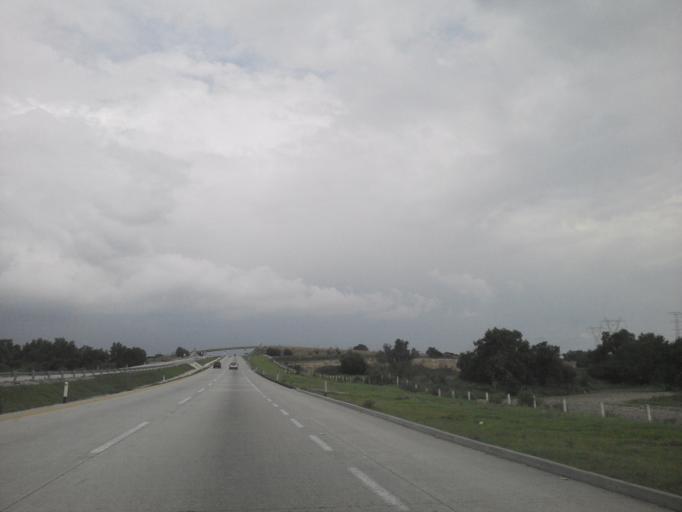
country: MX
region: Mexico
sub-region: Apaxco
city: Colonia Juarez
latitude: 19.9827
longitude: -99.1202
